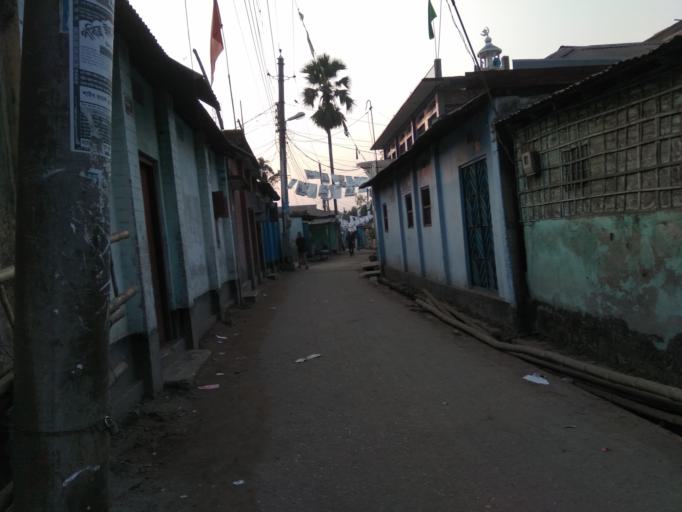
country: BD
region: Rangpur Division
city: Rangpur
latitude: 25.7287
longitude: 89.2626
